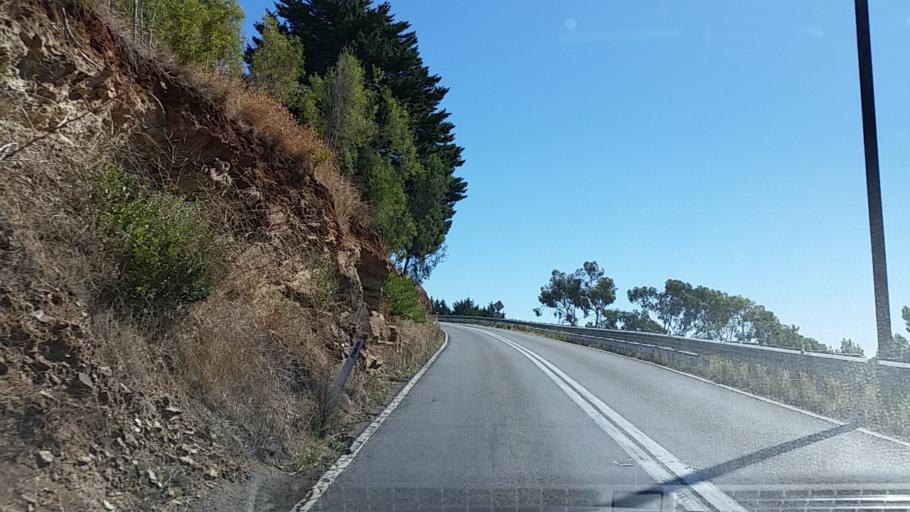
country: AU
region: South Australia
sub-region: Burnside
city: Beaumont
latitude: -34.9451
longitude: 138.6724
